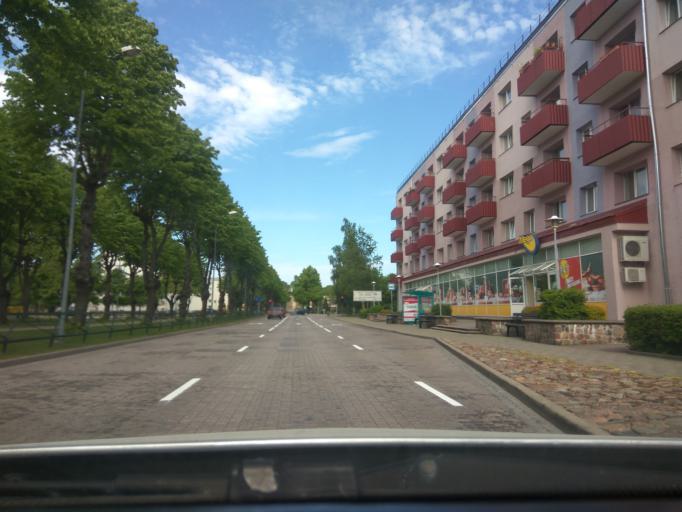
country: LV
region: Ventspils
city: Ventspils
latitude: 57.3921
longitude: 21.5751
